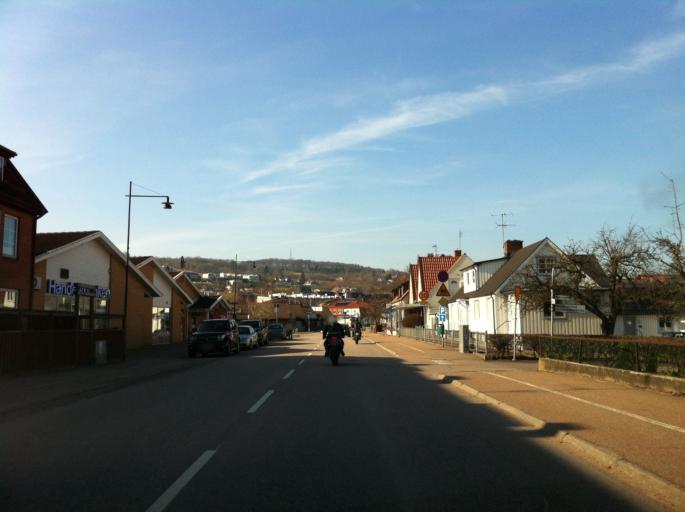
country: SE
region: Skane
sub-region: Bastads Kommun
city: Bastad
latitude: 56.4271
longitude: 12.8500
